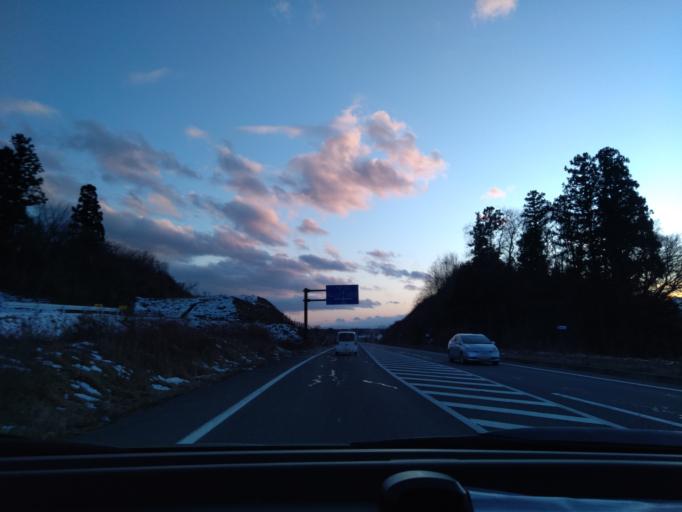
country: JP
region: Iwate
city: Hanamaki
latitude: 39.3841
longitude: 141.1434
